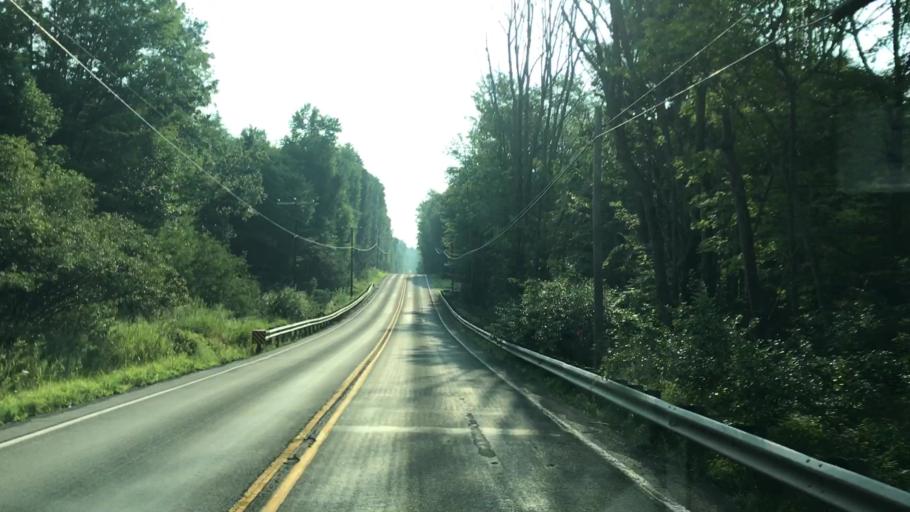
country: US
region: Pennsylvania
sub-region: Lackawanna County
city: Dalton
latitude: 41.5992
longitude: -75.6985
